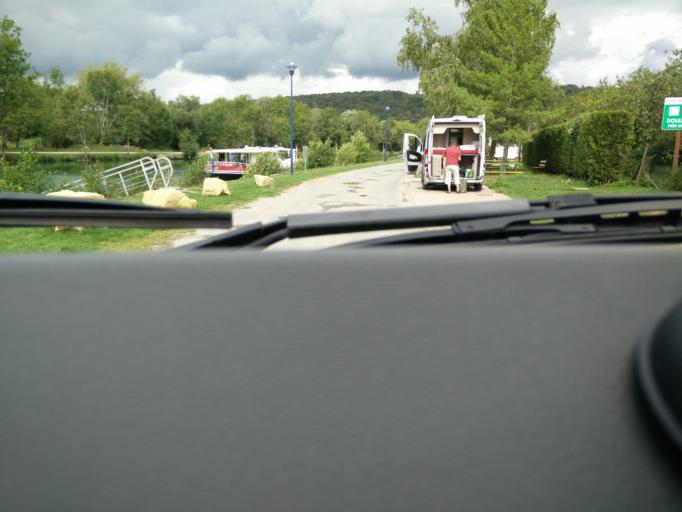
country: FR
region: Lorraine
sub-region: Departement de la Meuse
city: Stenay
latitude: 49.3882
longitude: 5.1788
